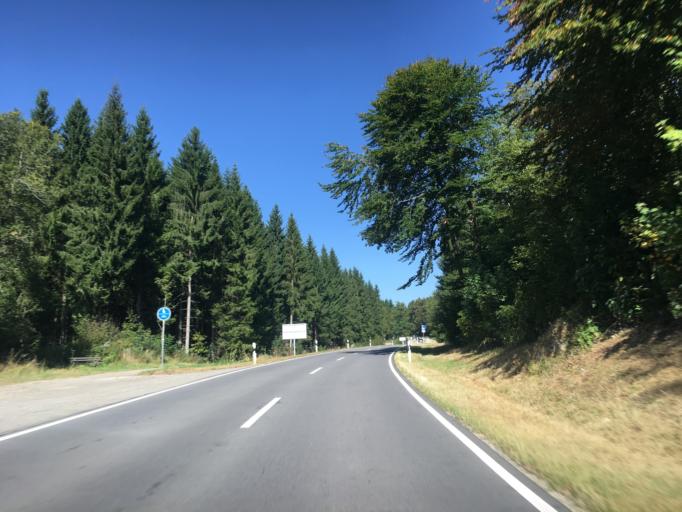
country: DE
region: Baden-Wuerttemberg
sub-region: Tuebingen Region
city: Munsingen
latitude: 48.3891
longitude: 9.4873
